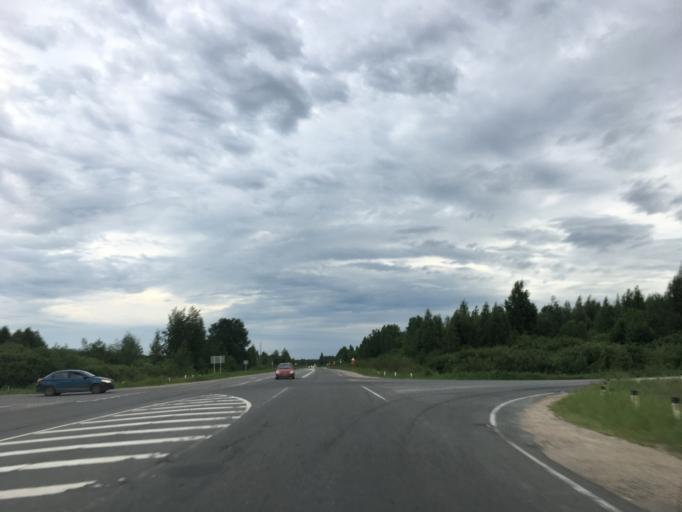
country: RU
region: Pskov
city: Pskov
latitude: 57.8469
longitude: 28.3907
